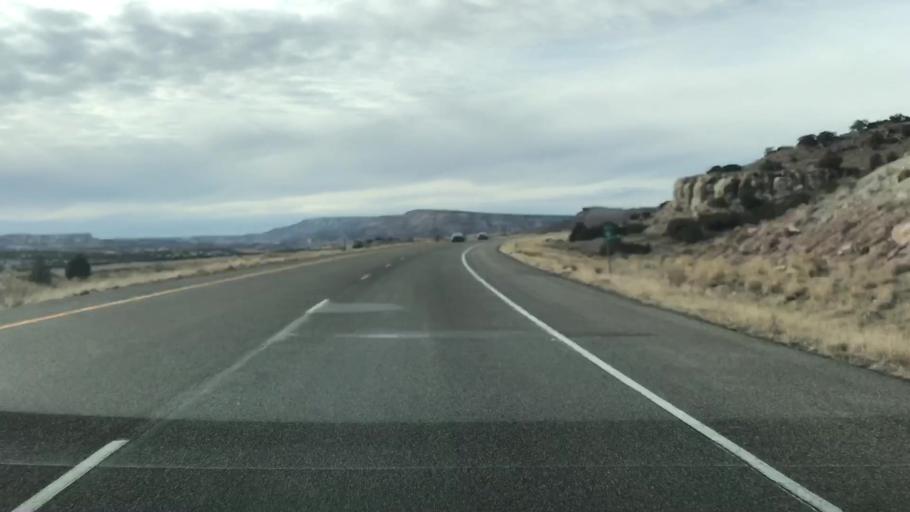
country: US
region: Colorado
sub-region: Mesa County
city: Loma
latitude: 39.2124
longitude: -108.9698
